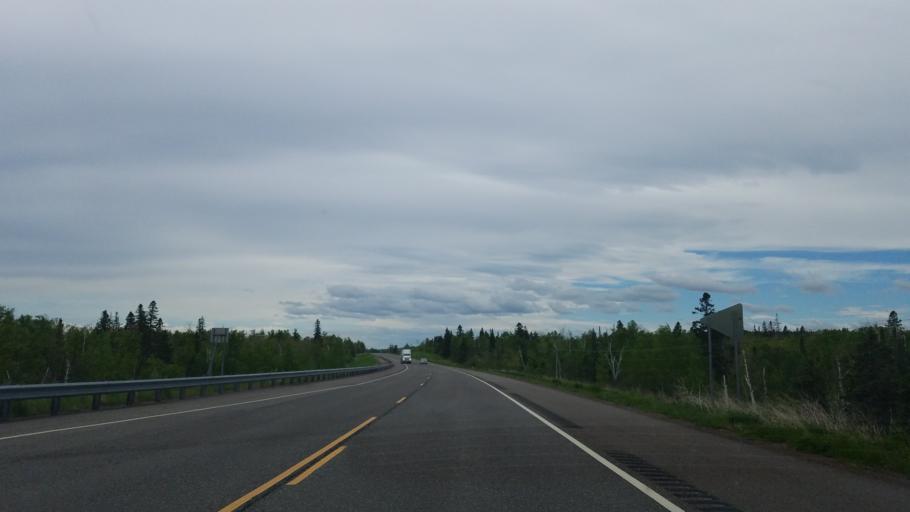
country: US
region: Minnesota
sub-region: Lake County
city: Silver Bay
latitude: 47.1982
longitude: -91.3834
